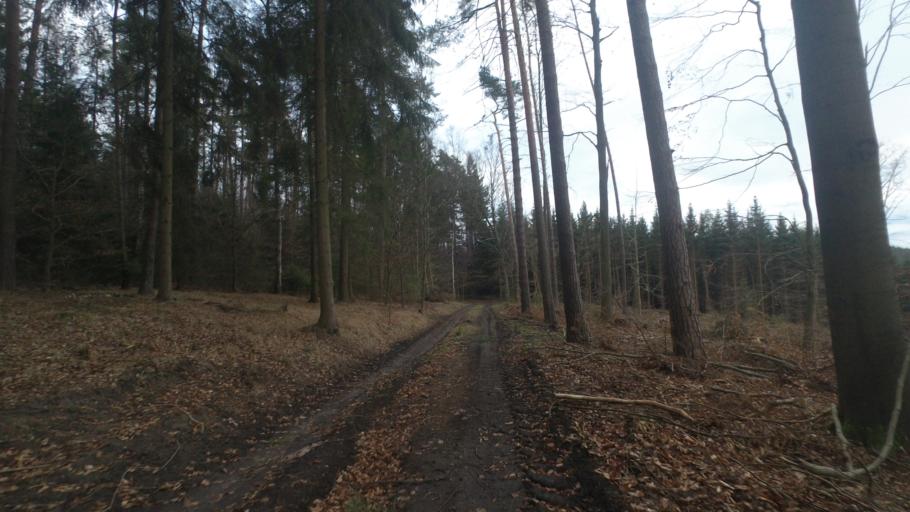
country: DE
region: Thuringia
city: Konitz
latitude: 50.7045
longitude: 11.4819
